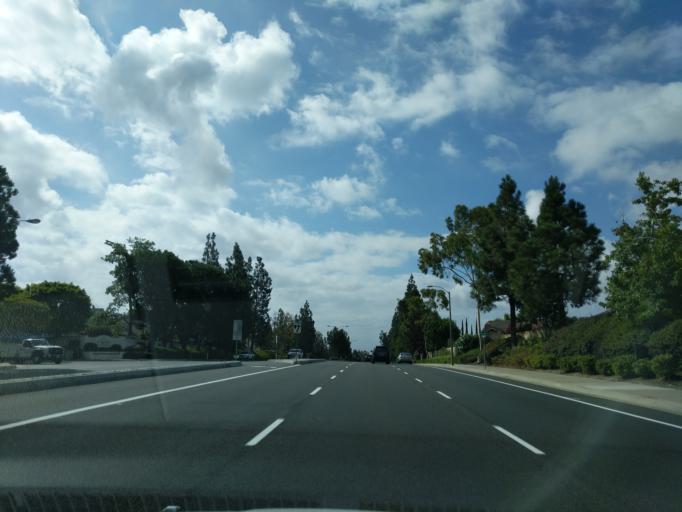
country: US
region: California
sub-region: Orange County
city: Laguna Niguel
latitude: 33.5327
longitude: -117.6850
